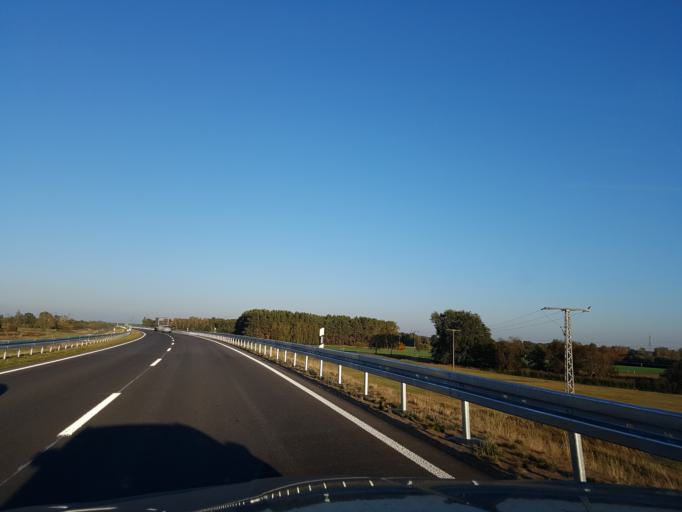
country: DE
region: Brandenburg
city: Bad Liebenwerda
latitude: 51.5033
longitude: 13.4021
